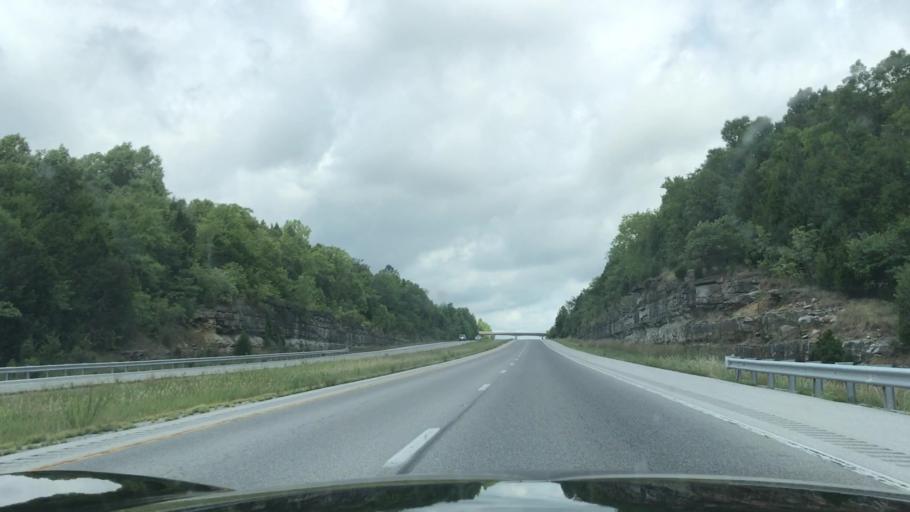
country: US
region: Kentucky
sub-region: Warren County
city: Bowling Green
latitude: 37.0233
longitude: -86.5296
